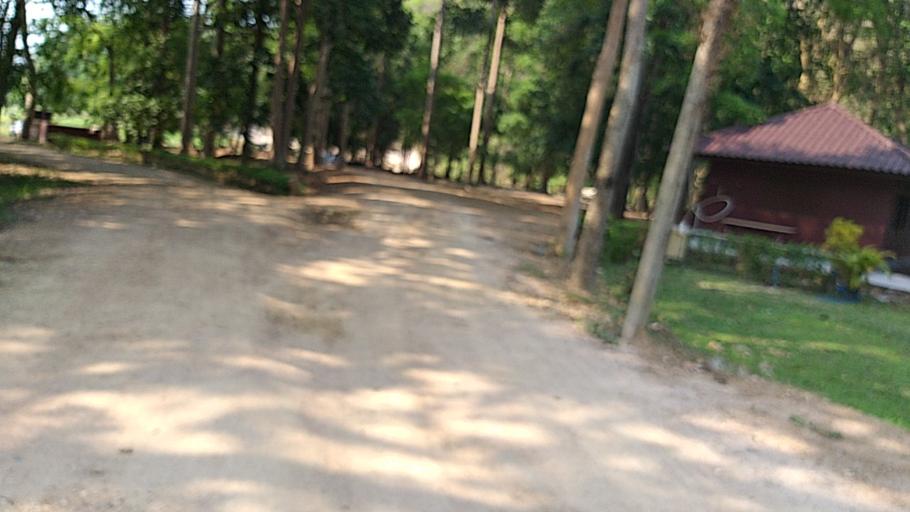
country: TH
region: Sara Buri
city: Wihan Daeng
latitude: 14.4408
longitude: 100.9606
